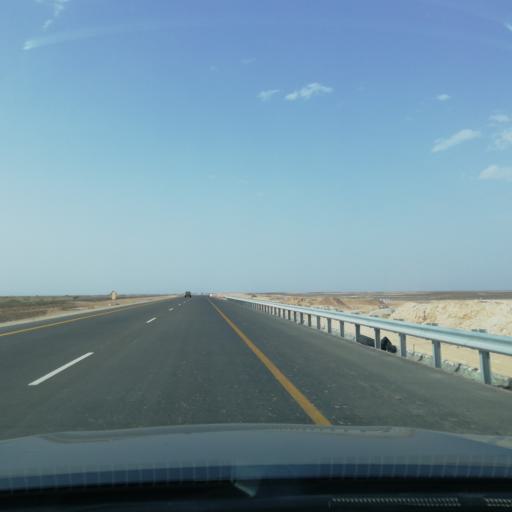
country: OM
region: Muhafazat ad Dakhiliyah
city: Adam
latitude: 22.1040
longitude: 57.5209
